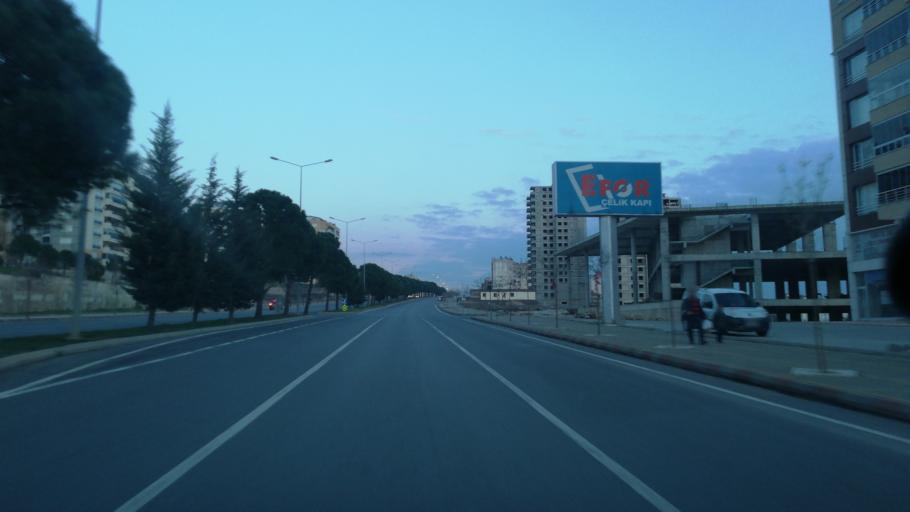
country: TR
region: Kahramanmaras
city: Kahramanmaras
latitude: 37.5977
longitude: 36.8449
